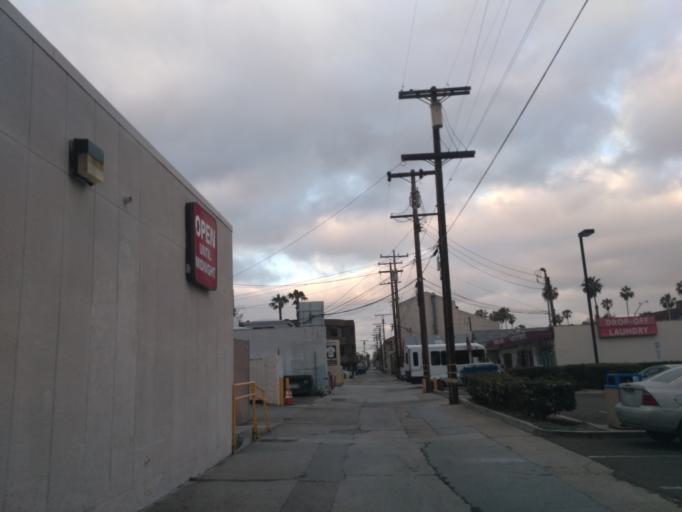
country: US
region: California
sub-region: San Diego County
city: La Jolla
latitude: 32.7954
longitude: -117.2543
